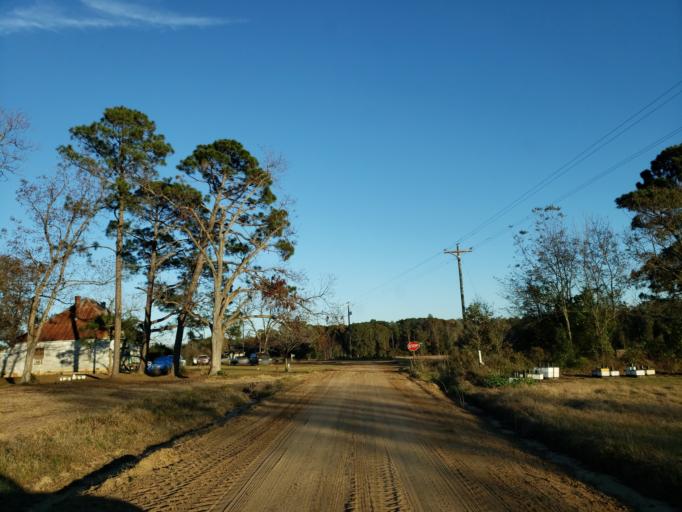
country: US
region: Georgia
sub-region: Dooly County
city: Vienna
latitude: 32.1442
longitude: -83.7425
